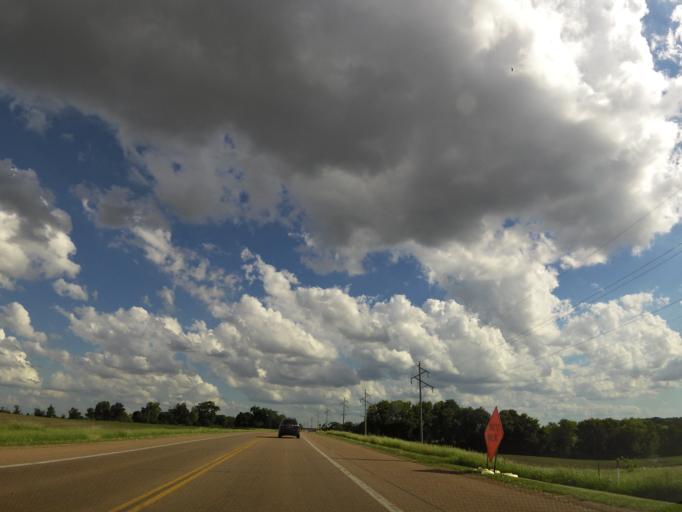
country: US
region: Minnesota
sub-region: Carver County
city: Waconia
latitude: 44.8461
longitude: -93.8189
